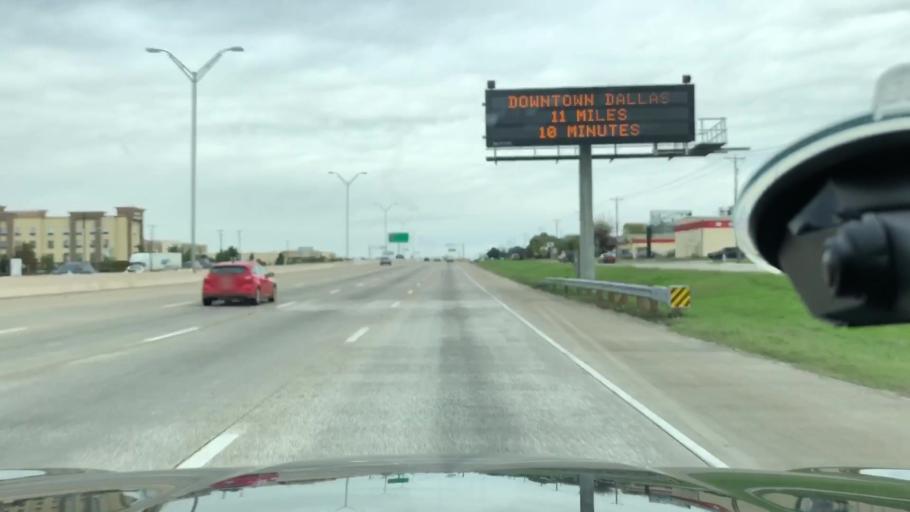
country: US
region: Texas
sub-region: Dallas County
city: DeSoto
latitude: 32.6248
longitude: -96.8230
